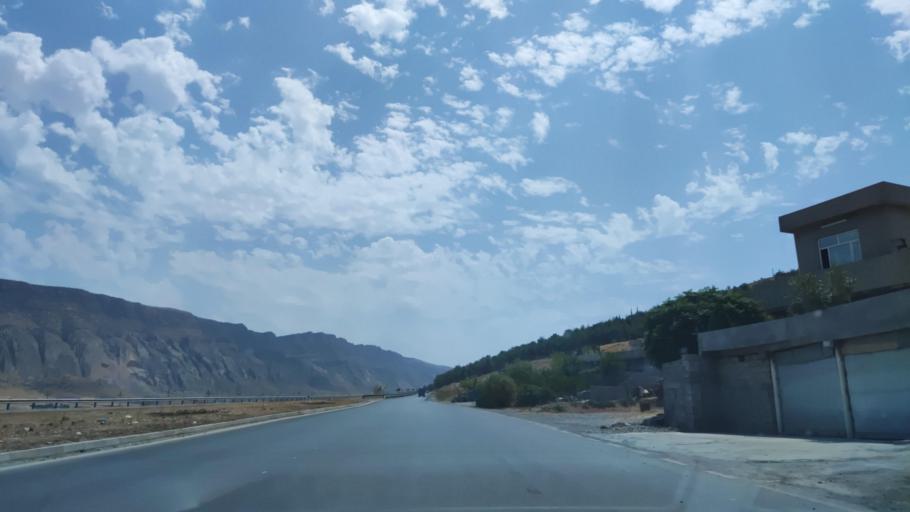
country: IQ
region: Arbil
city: Shaqlawah
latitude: 36.4925
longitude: 44.3707
